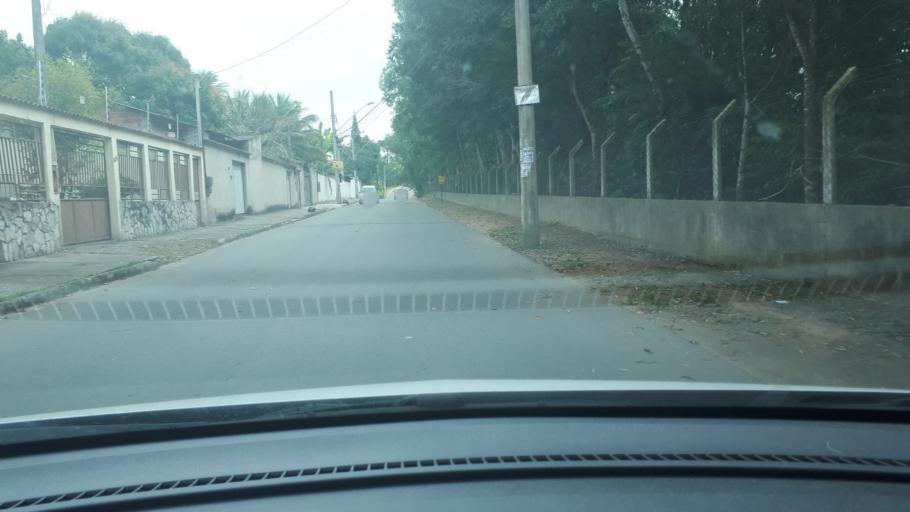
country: BR
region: Espirito Santo
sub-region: Serra
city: Serra
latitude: -20.1482
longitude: -40.1910
